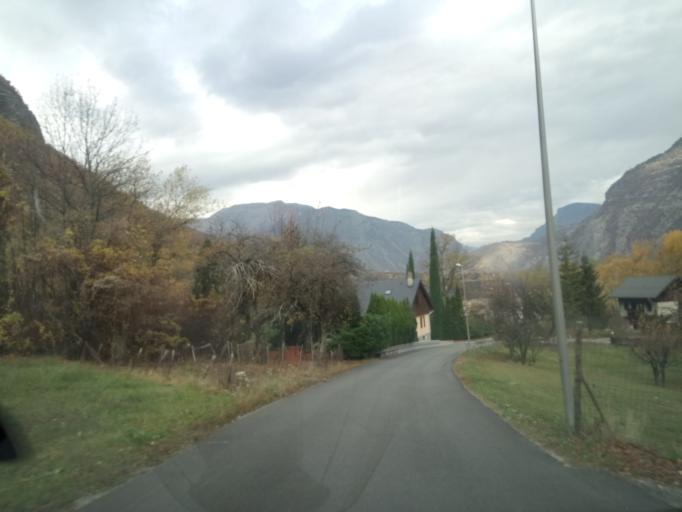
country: FR
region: Rhone-Alpes
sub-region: Departement de la Savoie
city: Villargondran
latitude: 45.2508
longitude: 6.3897
